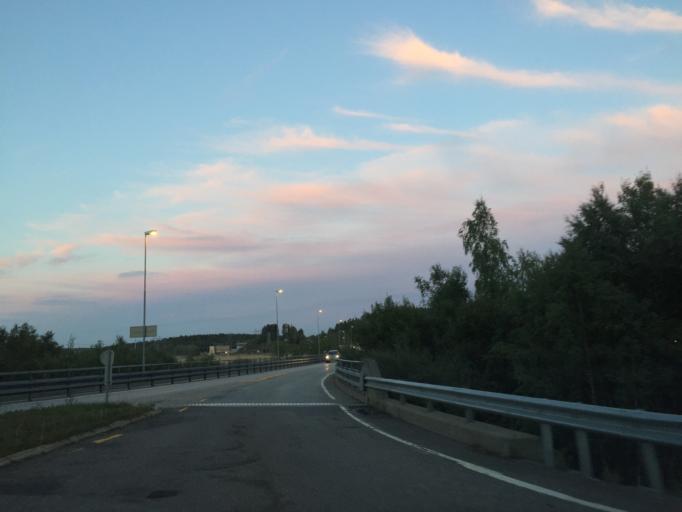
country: NO
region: Akershus
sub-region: Vestby
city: Vestby
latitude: 59.5170
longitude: 10.7221
